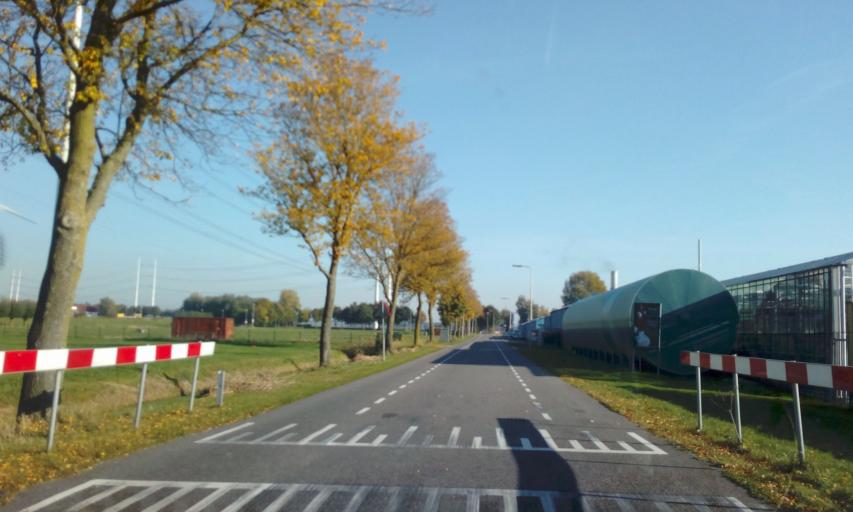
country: NL
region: South Holland
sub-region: Gemeente Zoetermeer
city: Zoetermeer
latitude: 52.0311
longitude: 4.4995
